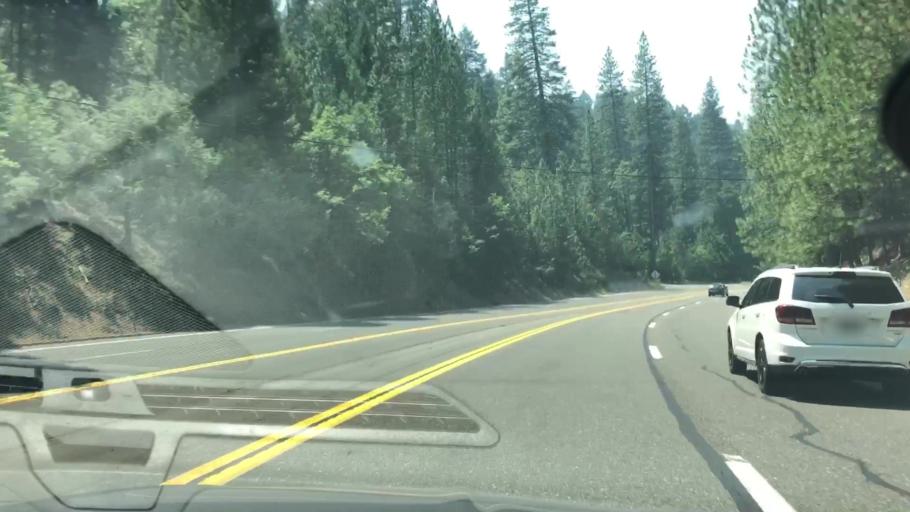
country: US
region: California
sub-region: El Dorado County
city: Pollock Pines
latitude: 38.7595
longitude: -120.5176
